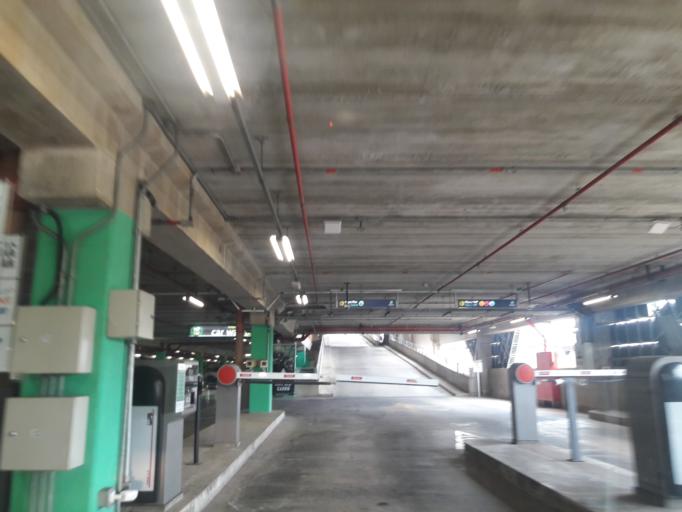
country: BR
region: Sao Paulo
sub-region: Indaiatuba
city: Indaiatuba
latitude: -23.0099
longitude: -47.1459
